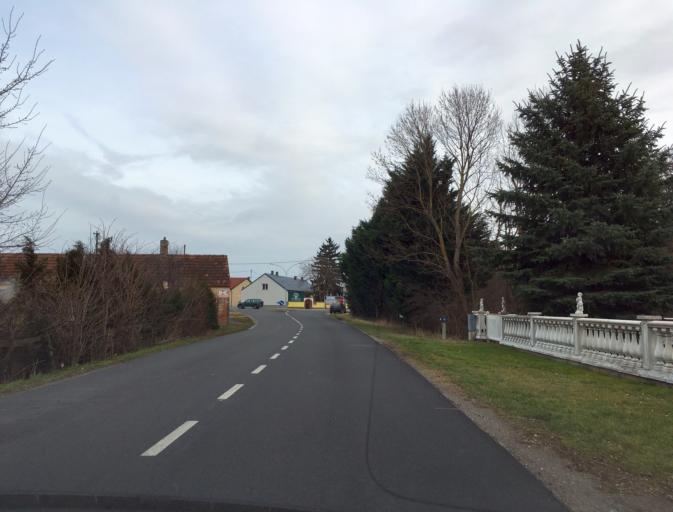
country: AT
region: Lower Austria
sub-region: Politischer Bezirk Ganserndorf
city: Engelhartstetten
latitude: 48.2199
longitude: 16.8994
